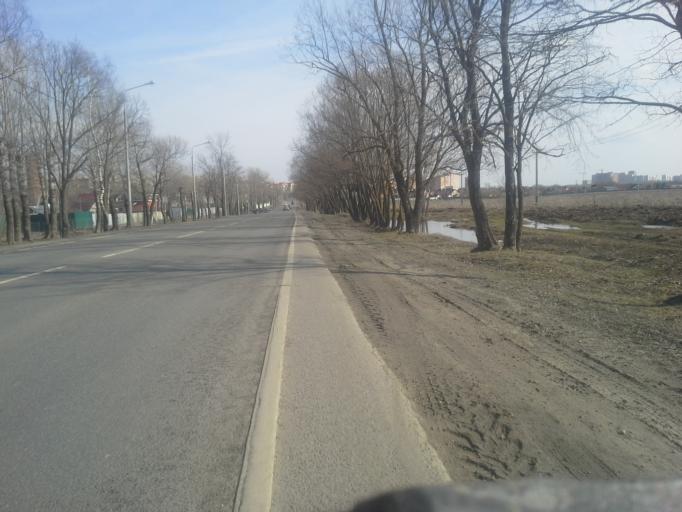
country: RU
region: Moskovskaya
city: Shcherbinka
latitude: 55.4779
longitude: 37.5285
